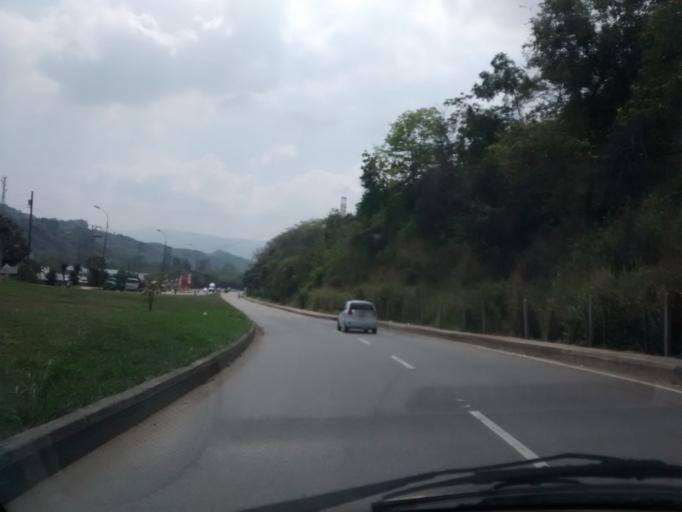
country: CO
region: Santander
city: Bucaramanga
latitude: 7.0915
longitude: -73.1284
